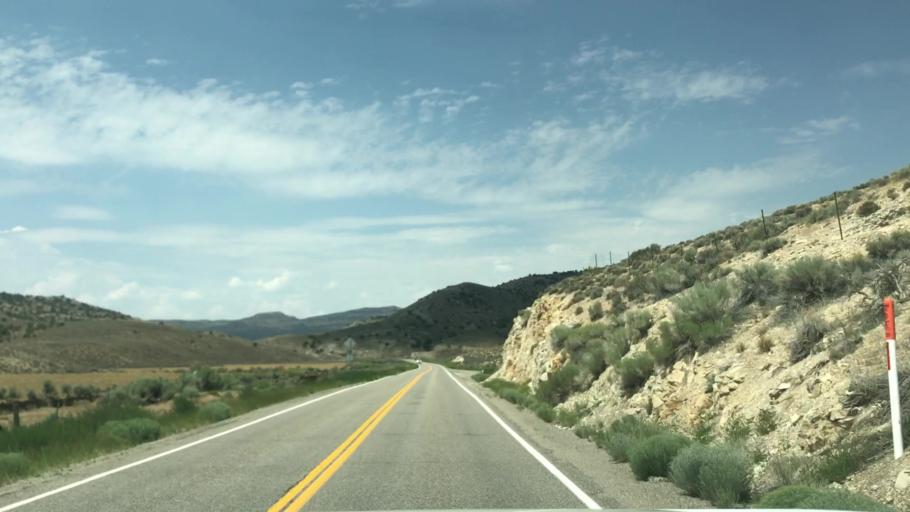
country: US
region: Nevada
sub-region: White Pine County
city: Ely
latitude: 39.3520
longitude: -115.3691
